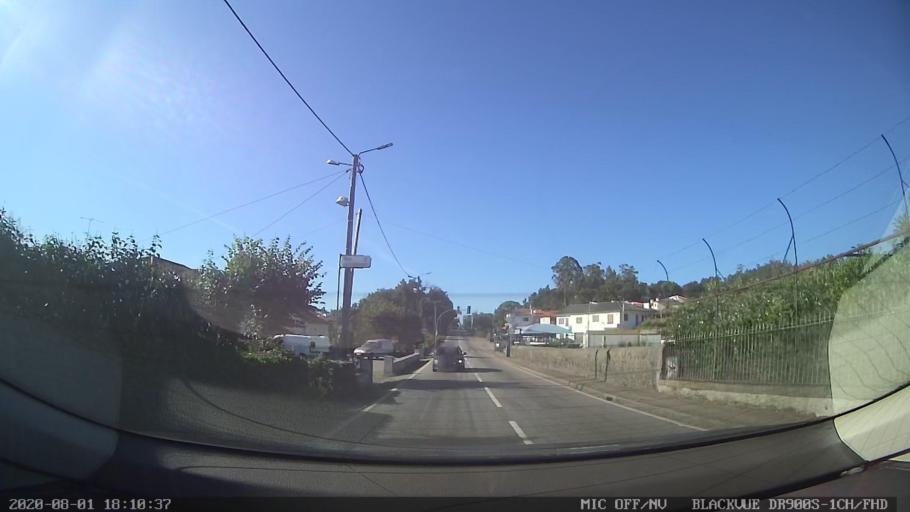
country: PT
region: Porto
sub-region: Santo Tirso
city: Sao Miguel do Couto
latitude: 41.3023
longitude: -8.4710
